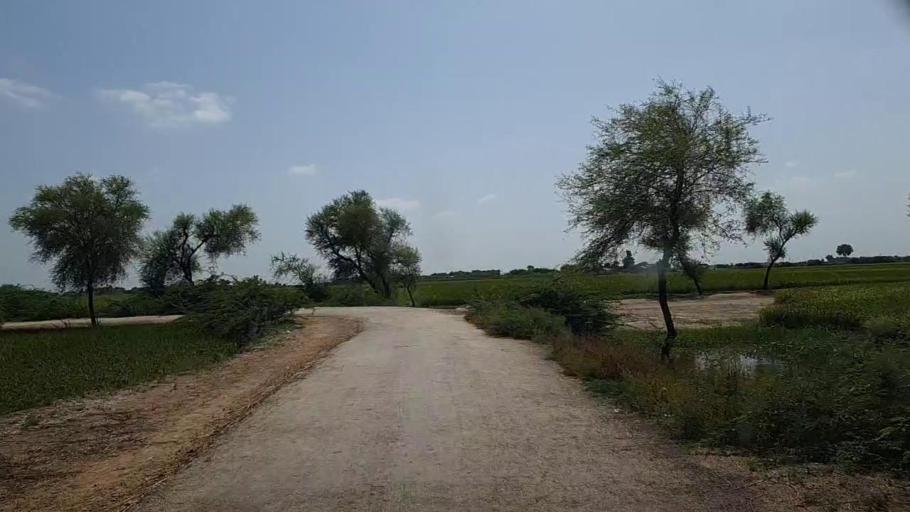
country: PK
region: Sindh
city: Kario
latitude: 24.6436
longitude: 68.5640
